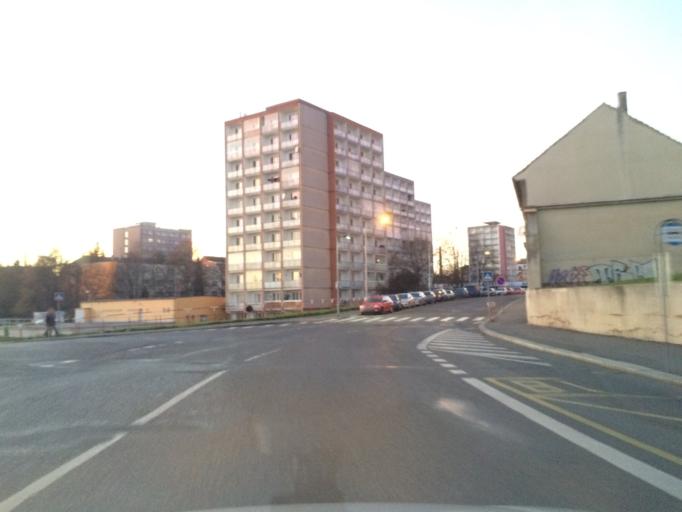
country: CZ
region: Central Bohemia
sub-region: Okres Kladno
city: Slany
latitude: 50.2281
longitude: 14.0819
